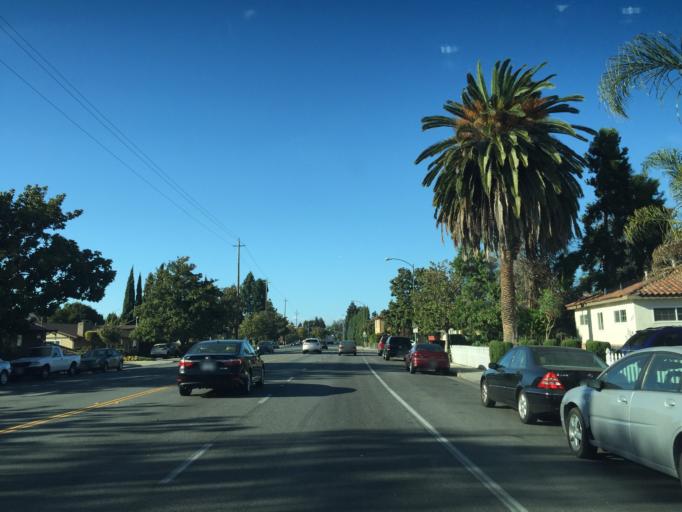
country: US
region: California
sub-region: Santa Clara County
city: Mountain View
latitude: 37.4166
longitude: -122.0930
